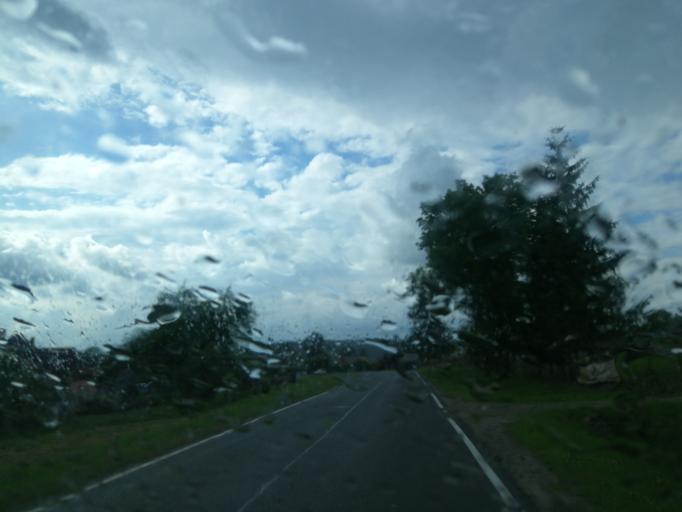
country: PL
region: Subcarpathian Voivodeship
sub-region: Powiat leski
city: Uherce Mineralne
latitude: 49.4584
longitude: 22.4097
